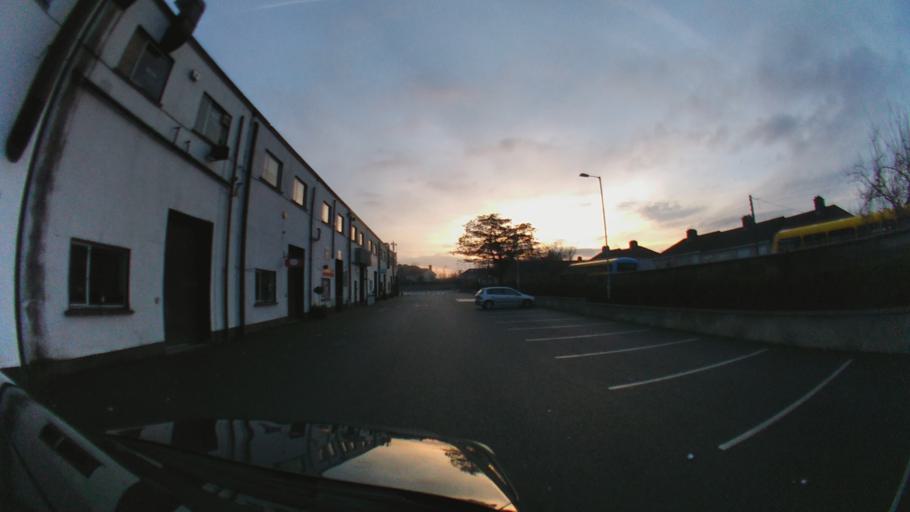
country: IE
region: Leinster
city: Artane
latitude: 53.3859
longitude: -6.2140
